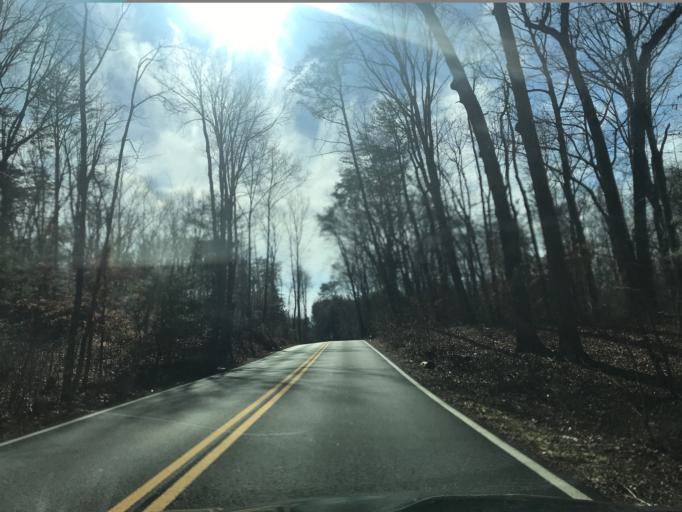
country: US
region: Maryland
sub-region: Charles County
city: Indian Head
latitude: 38.4957
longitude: -77.1583
